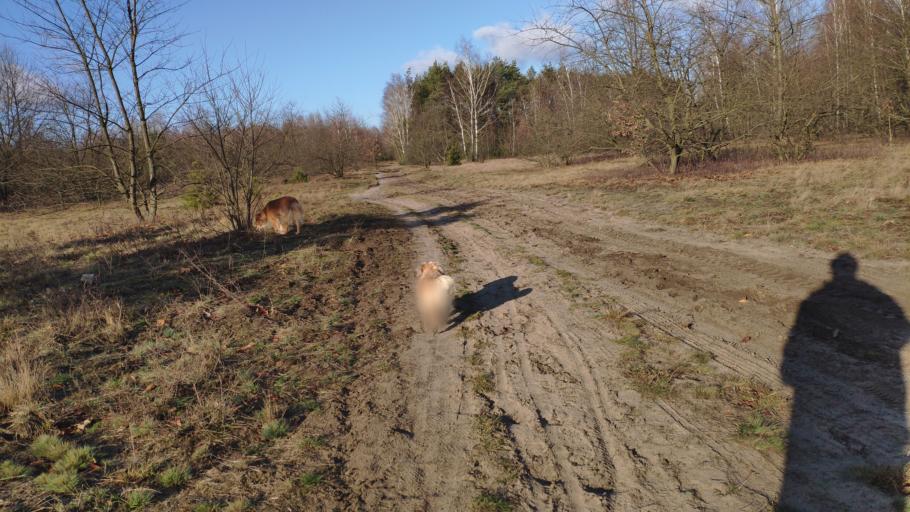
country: PL
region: Lodz Voivodeship
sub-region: Powiat pabianicki
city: Ksawerow
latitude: 51.7275
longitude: 19.4123
